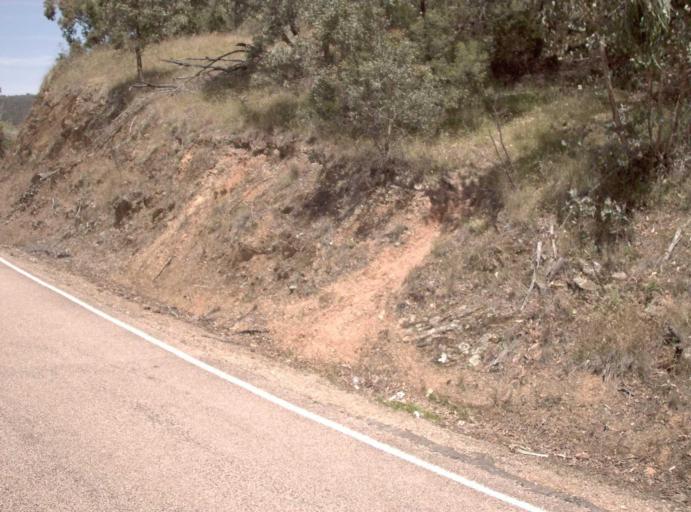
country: AU
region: Victoria
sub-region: East Gippsland
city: Bairnsdale
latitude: -37.4221
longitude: 147.8352
